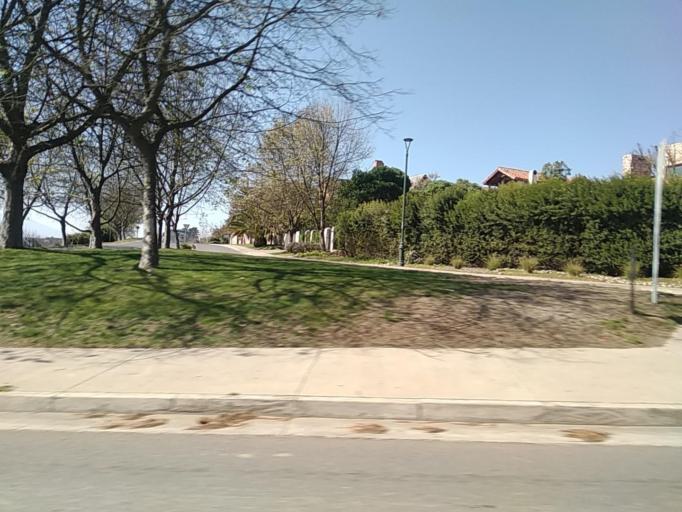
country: CL
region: Valparaiso
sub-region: Provincia de Valparaiso
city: Vina del Mar
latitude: -32.9439
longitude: -71.5375
